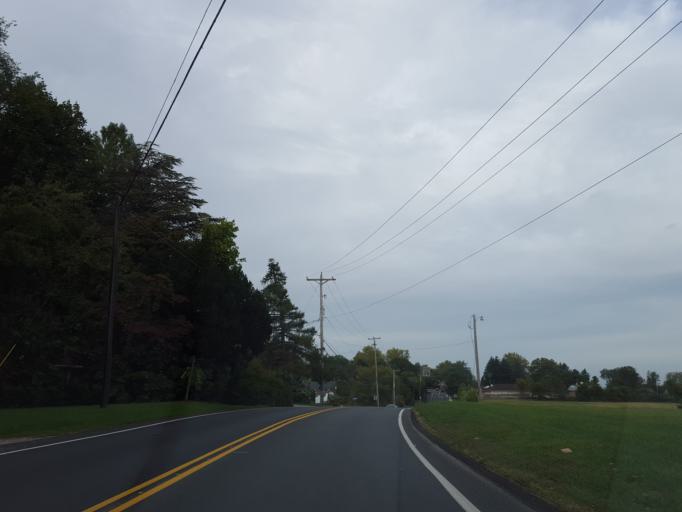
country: US
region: Pennsylvania
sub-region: York County
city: Spry
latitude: 39.9097
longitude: -76.7083
